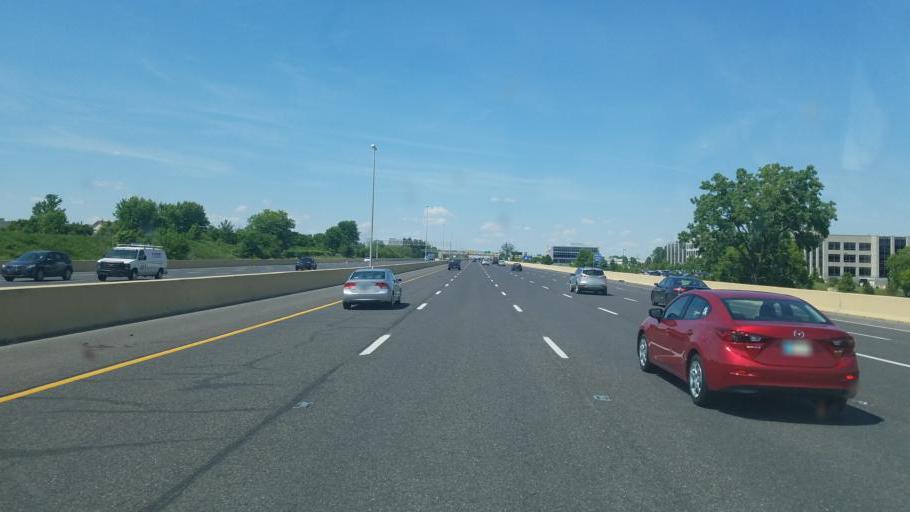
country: US
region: Indiana
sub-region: Boone County
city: Zionsville
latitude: 39.8877
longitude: -86.2694
